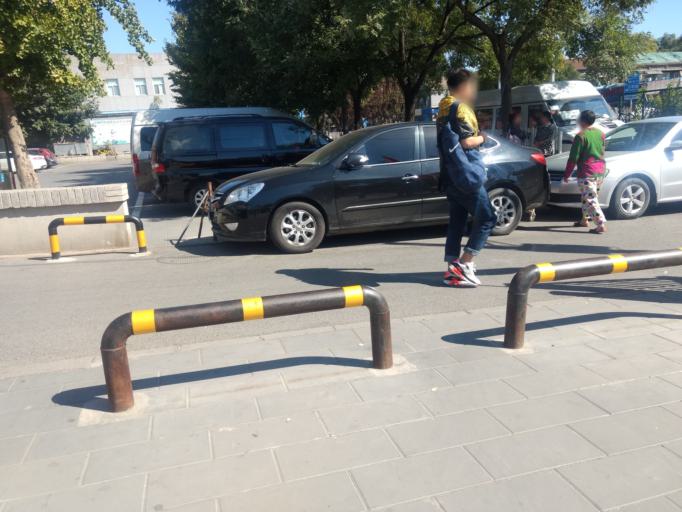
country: CN
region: Beijing
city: Beijing
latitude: 39.8886
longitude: 116.3825
